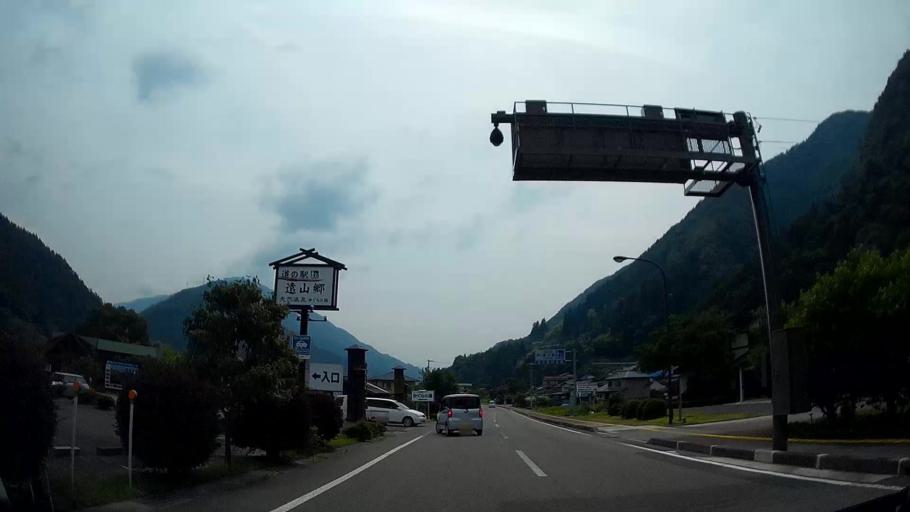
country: JP
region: Nagano
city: Iida
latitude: 35.3214
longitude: 137.9300
